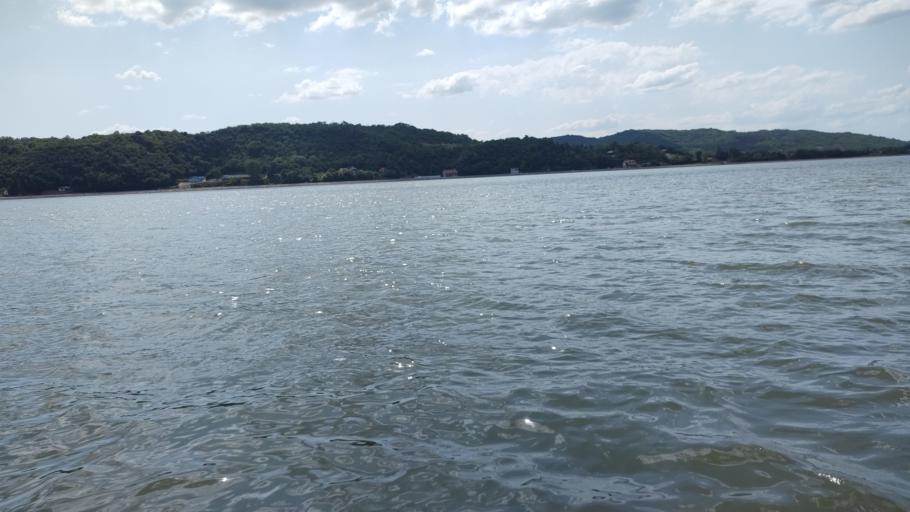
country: RS
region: Central Serbia
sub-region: Branicevski Okrug
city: Golubac
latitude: 44.6628
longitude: 21.6271
